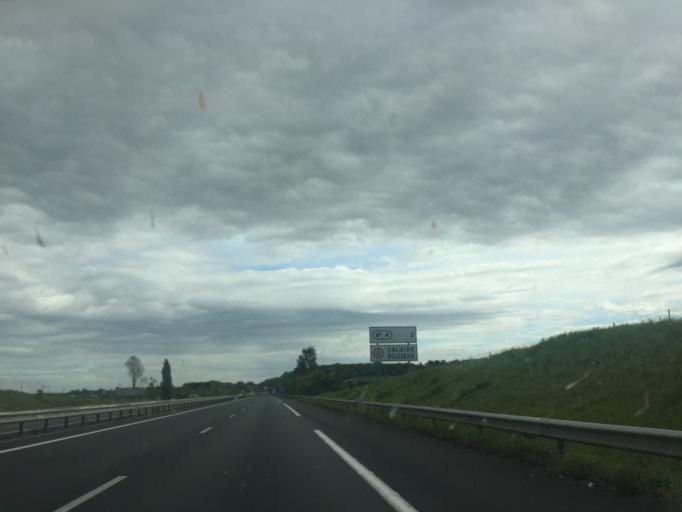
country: FR
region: Rhone-Alpes
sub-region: Departement du Rhone
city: Sathonay-Village
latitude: 45.8509
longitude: 4.9103
